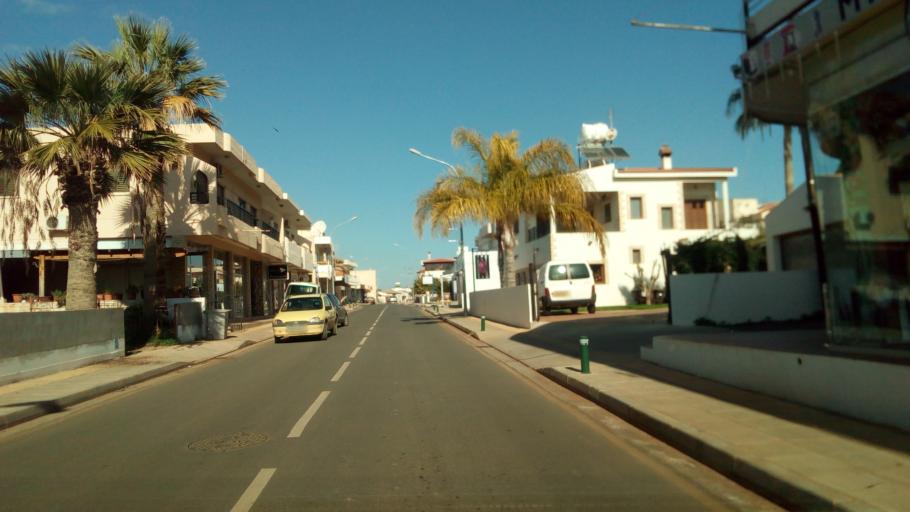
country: CY
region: Ammochostos
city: Avgorou
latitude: 35.0345
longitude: 33.8399
